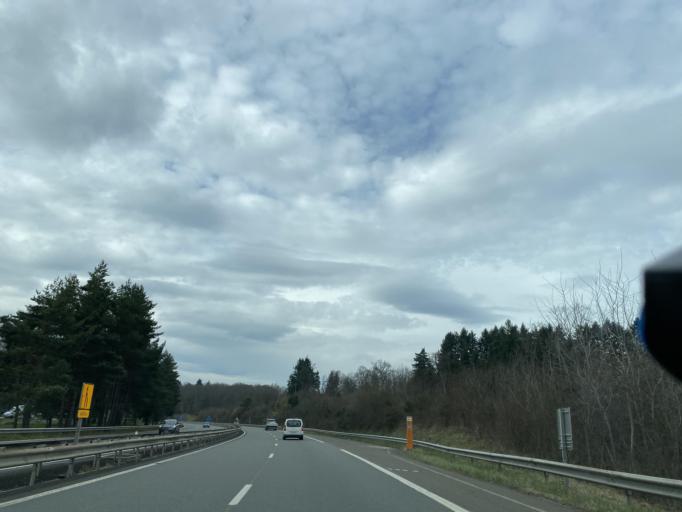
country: FR
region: Auvergne
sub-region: Departement du Puy-de-Dome
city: Saint-Remy-sur-Durolle
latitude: 45.8823
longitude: 3.5719
